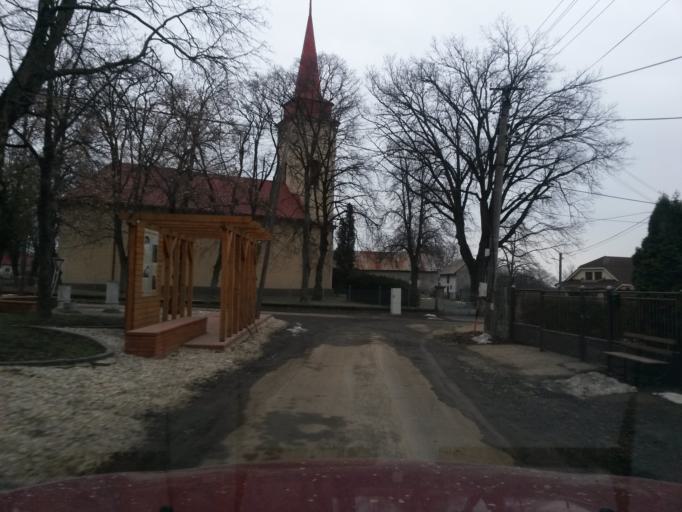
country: SK
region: Kosicky
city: Trebisov
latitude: 48.6814
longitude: 21.8146
